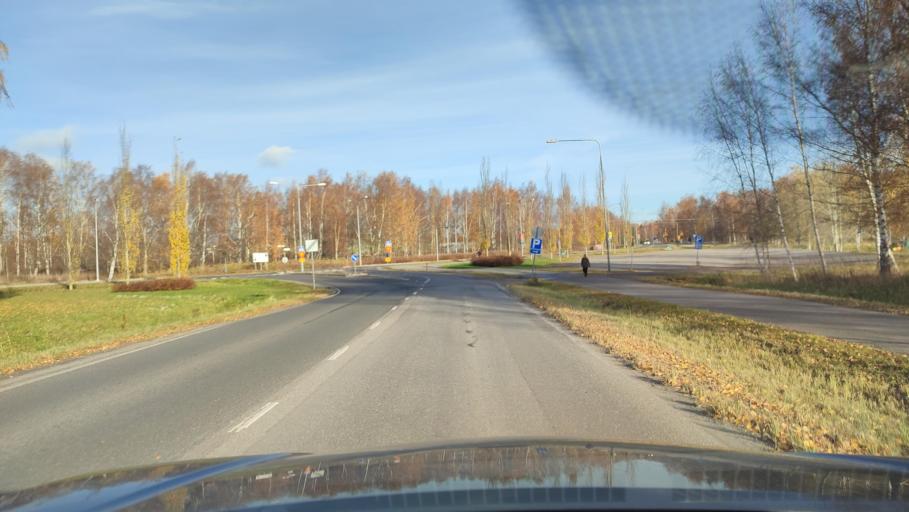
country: FI
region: Ostrobothnia
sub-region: Vaasa
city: Vaasa
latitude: 63.0875
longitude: 21.6466
